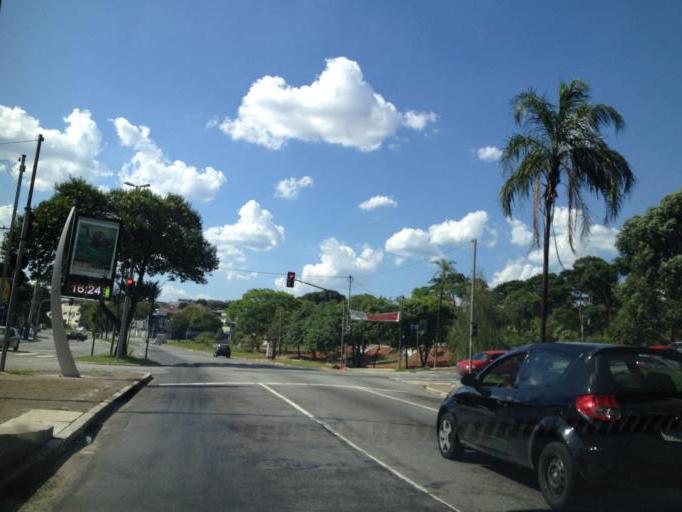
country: BR
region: Sao Paulo
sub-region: Guarulhos
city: Guarulhos
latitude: -23.5072
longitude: -46.5713
